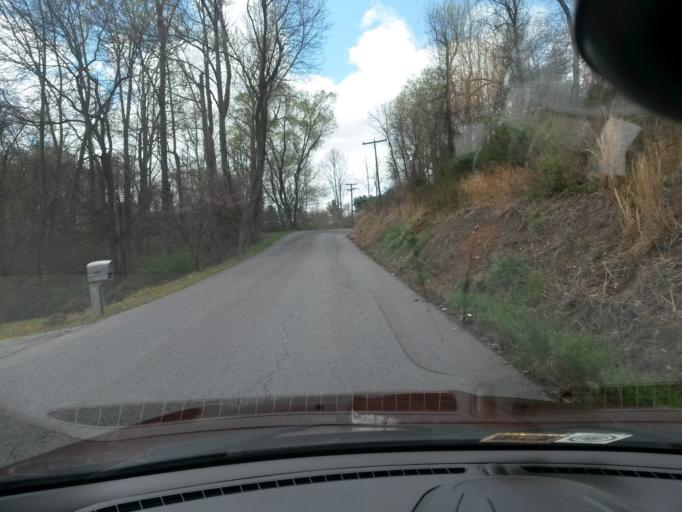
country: US
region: Virginia
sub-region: City of Lynchburg
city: West Lynchburg
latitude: 37.4049
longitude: -79.1899
